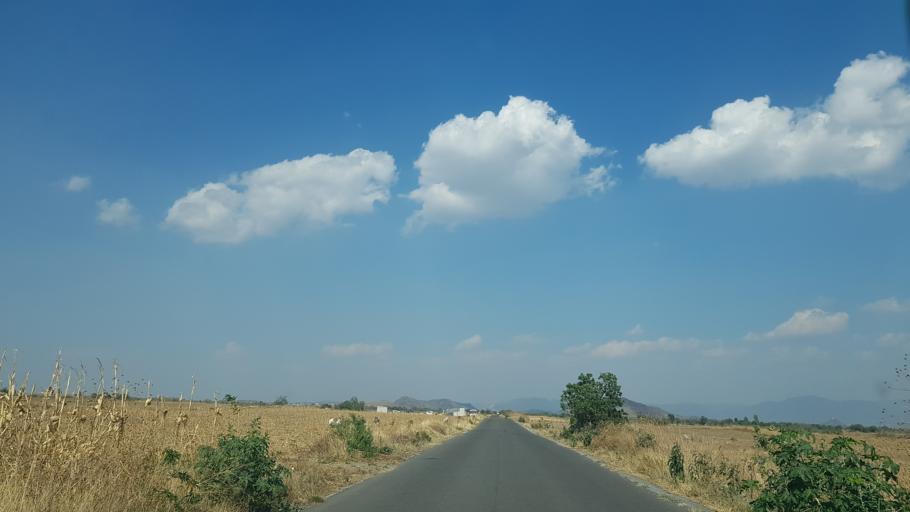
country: MX
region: Puebla
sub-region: Atlixco
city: Colonia Agricola de Ocotepec (Colonia San Jose)
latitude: 18.9205
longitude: -98.5166
